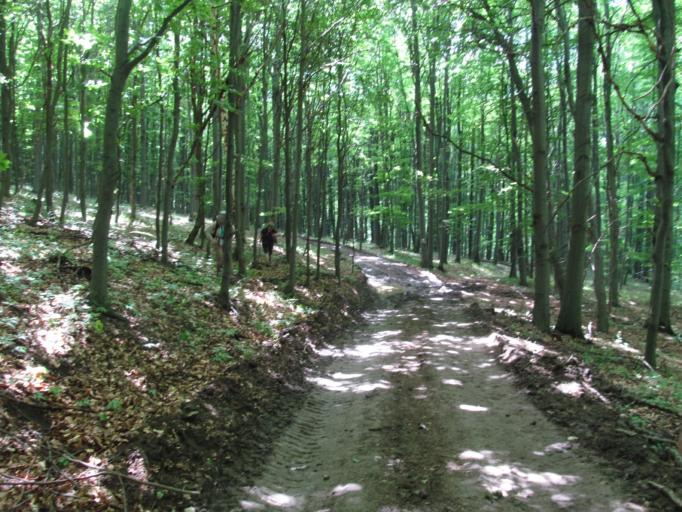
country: HU
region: Borsod-Abauj-Zemplen
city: Gonc
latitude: 48.5783
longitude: 21.4404
